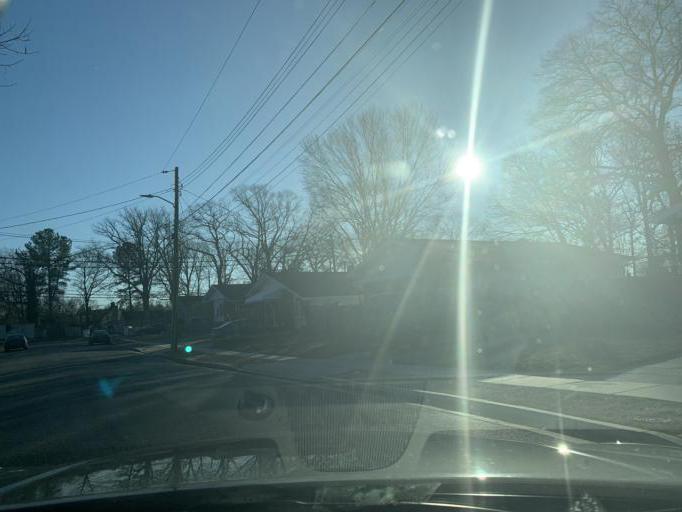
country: US
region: Maryland
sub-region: Anne Arundel County
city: Glen Burnie
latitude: 39.1519
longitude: -76.6241
